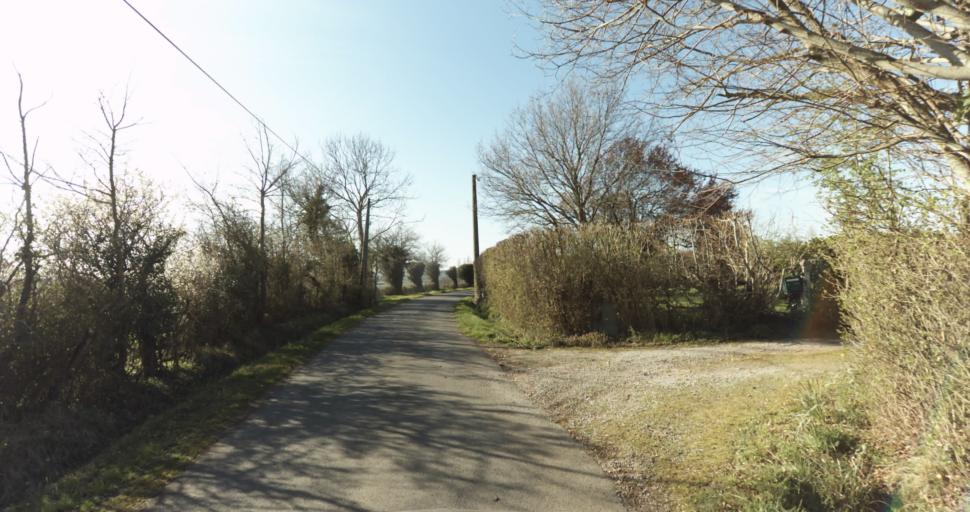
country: FR
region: Lower Normandy
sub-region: Departement du Calvados
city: Saint-Pierre-sur-Dives
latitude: 49.0460
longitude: 0.0321
